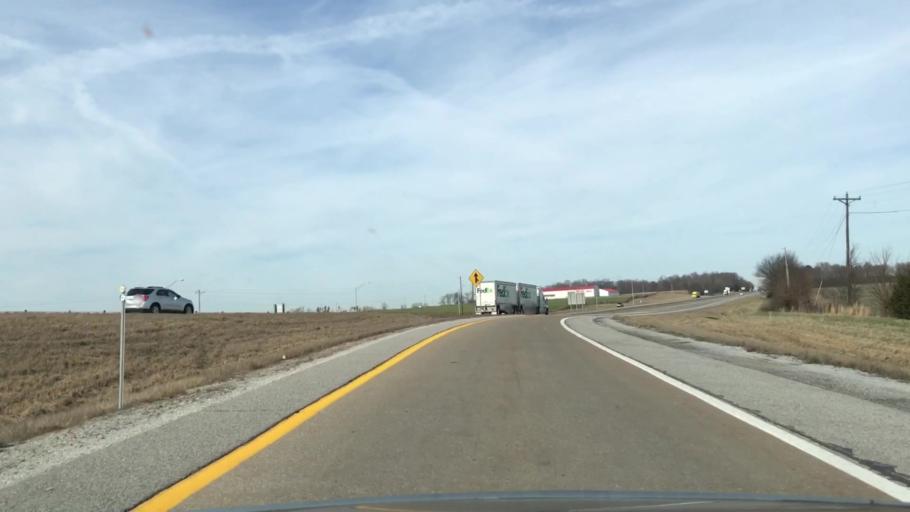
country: US
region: Kentucky
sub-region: Trigg County
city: Cadiz
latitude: 36.8844
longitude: -87.7351
